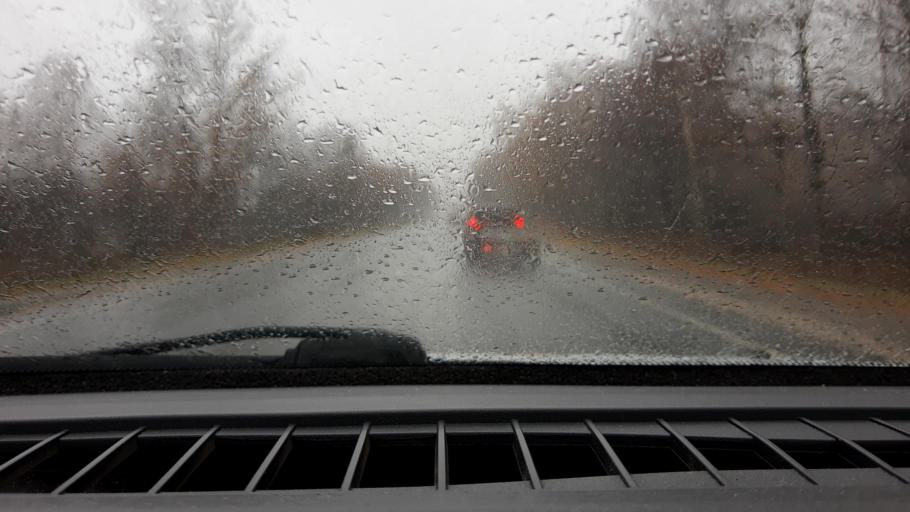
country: RU
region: Nizjnij Novgorod
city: Sitniki
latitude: 56.5325
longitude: 44.0232
